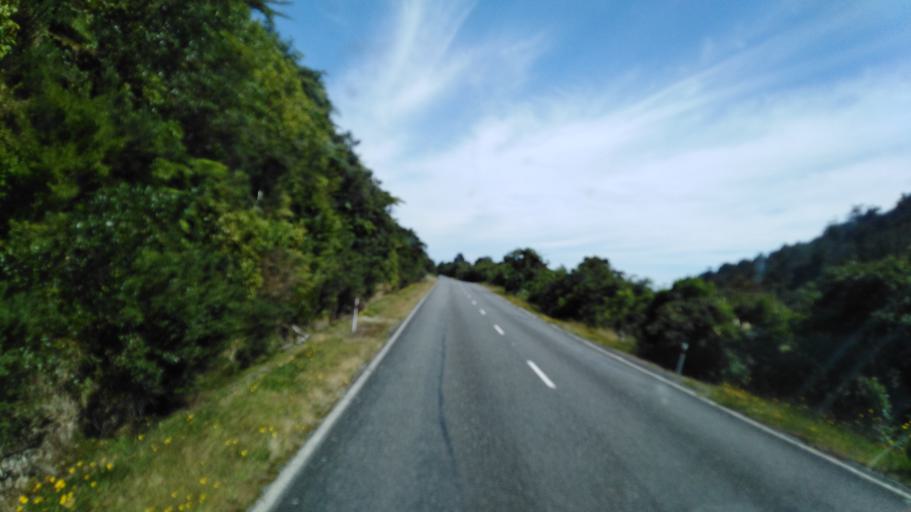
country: NZ
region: West Coast
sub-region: Buller District
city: Westport
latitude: -41.5312
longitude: 171.9513
